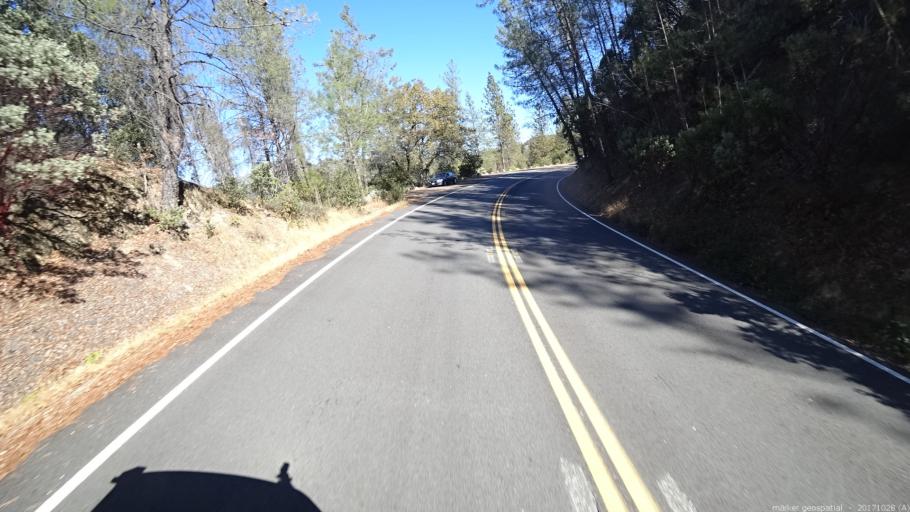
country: US
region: California
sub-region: Shasta County
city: Shasta
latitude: 40.6032
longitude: -122.5360
